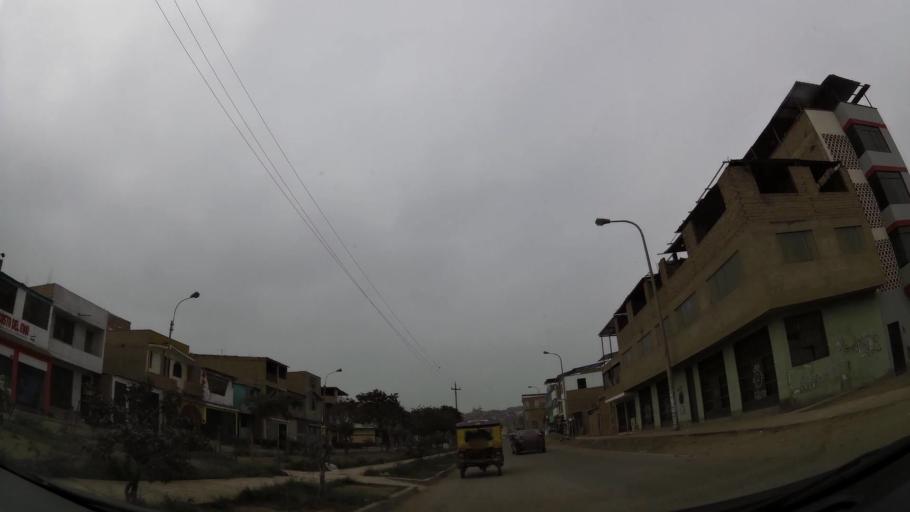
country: PE
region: Lima
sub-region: Lima
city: Surco
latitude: -12.2346
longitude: -76.9205
